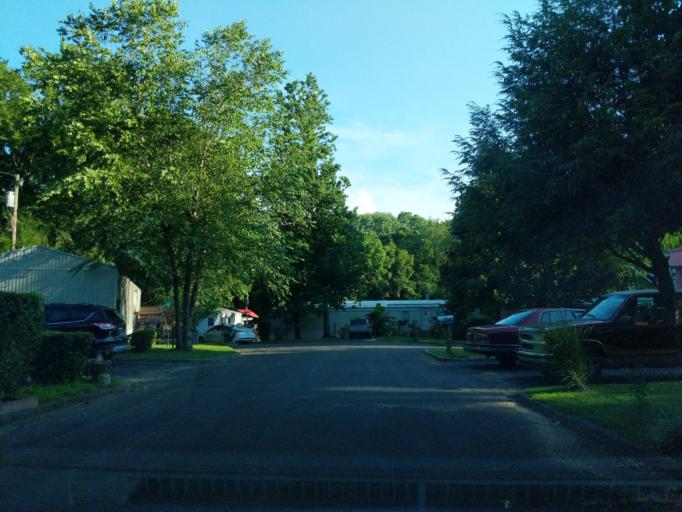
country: US
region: Tennessee
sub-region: Davidson County
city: Lakewood
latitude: 36.2589
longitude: -86.6279
